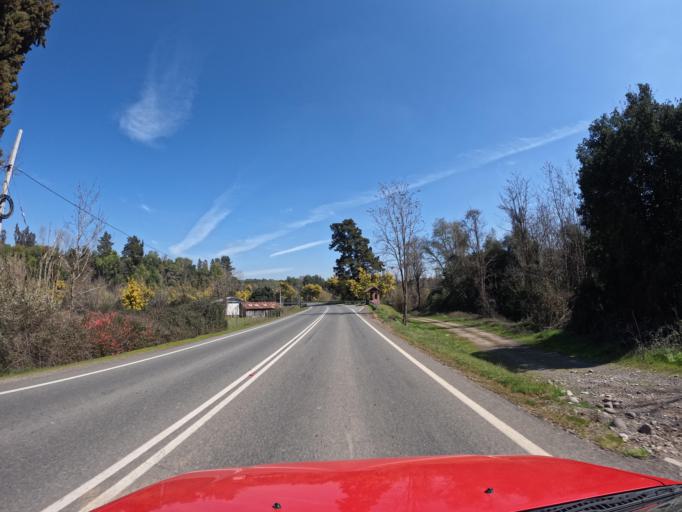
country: CL
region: Maule
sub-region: Provincia de Talca
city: San Clemente
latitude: -35.4675
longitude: -71.2736
